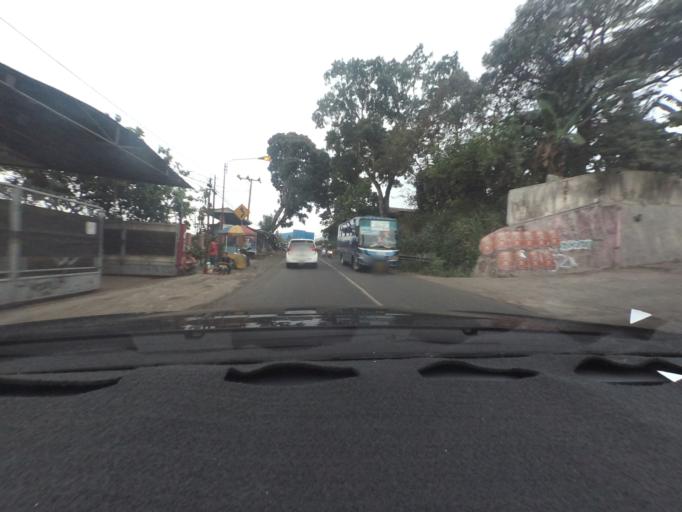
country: ID
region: West Java
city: Cicurug
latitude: -6.7990
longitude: 106.7758
